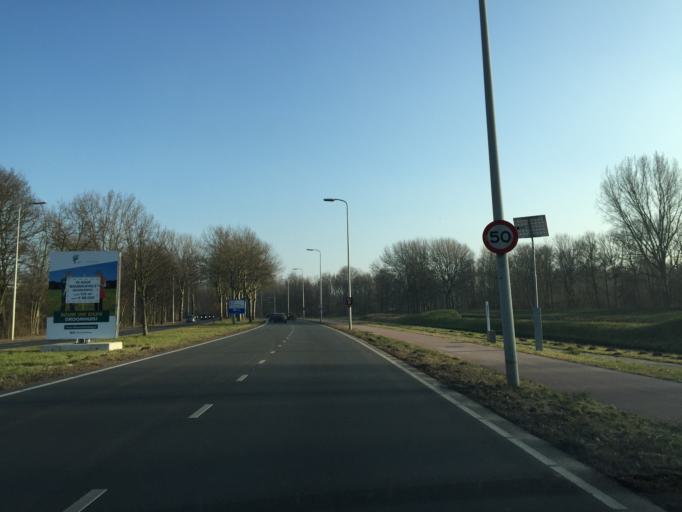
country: NL
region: South Holland
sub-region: Gemeente Westland
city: Poeldijk
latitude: 52.0456
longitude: 4.2339
